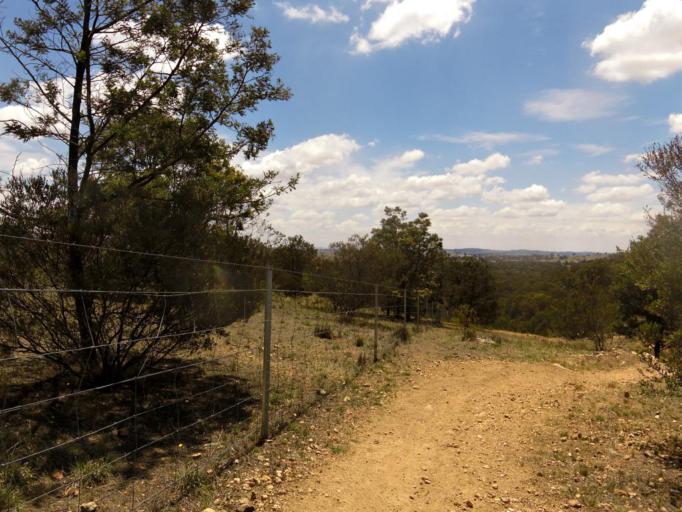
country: AU
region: Australian Capital Territory
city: Kaleen
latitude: -35.1425
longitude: 149.1469
